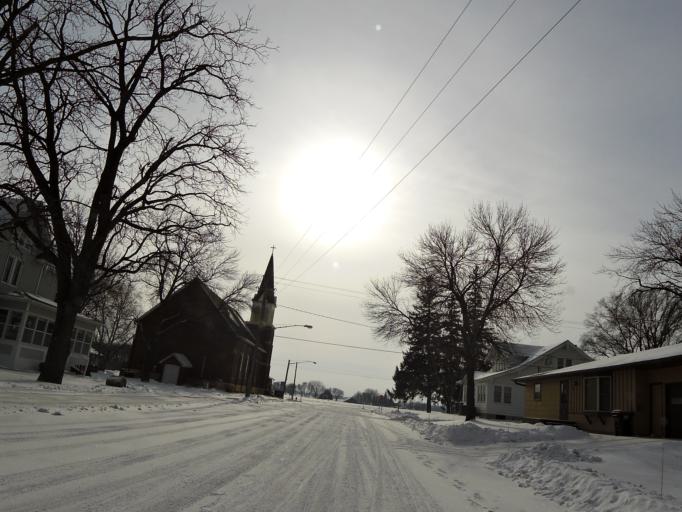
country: US
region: Minnesota
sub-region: Carver County
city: Mayer
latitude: 44.8854
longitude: -93.9638
